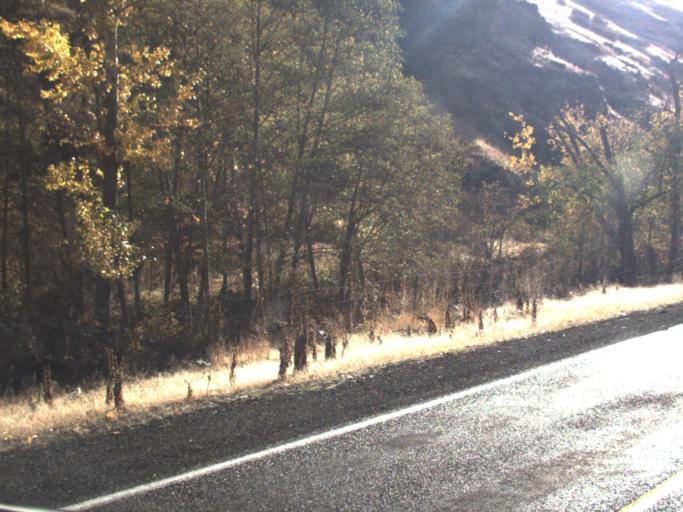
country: US
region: Washington
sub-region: Asotin County
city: Asotin
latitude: 46.0302
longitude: -117.2565
